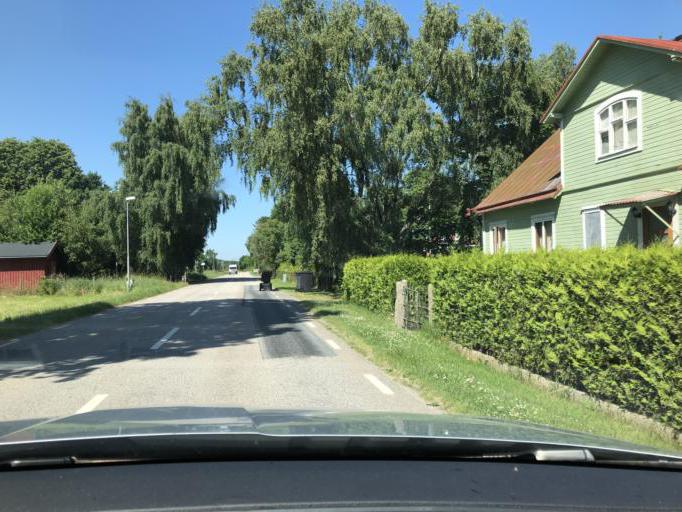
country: SE
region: Blekinge
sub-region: Solvesborgs Kommun
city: Soelvesborg
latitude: 56.1032
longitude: 14.6183
